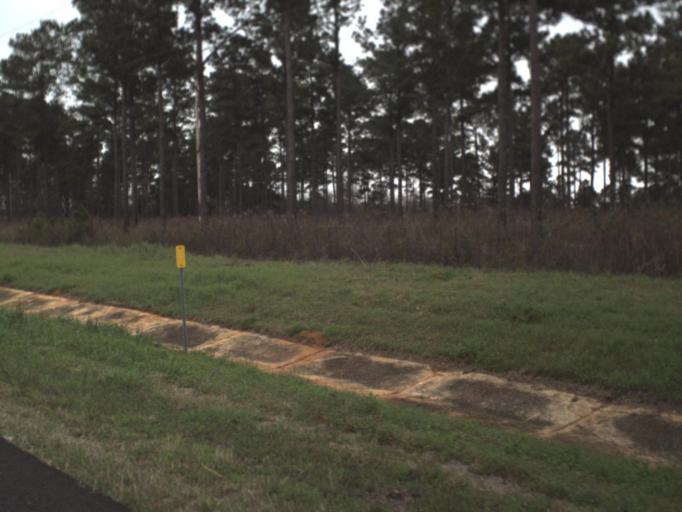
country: US
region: Florida
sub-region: Jefferson County
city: Monticello
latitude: 30.3976
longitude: -83.8761
